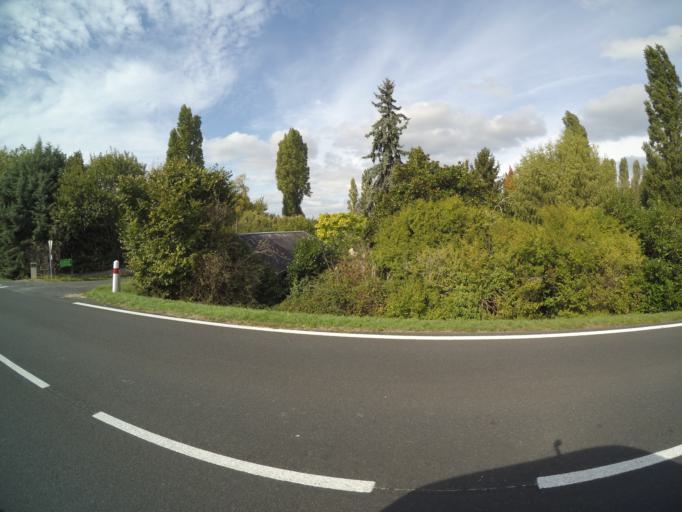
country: FR
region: Centre
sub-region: Departement d'Indre-et-Loire
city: La Chapelle-sur-Loire
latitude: 47.2538
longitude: 0.2410
